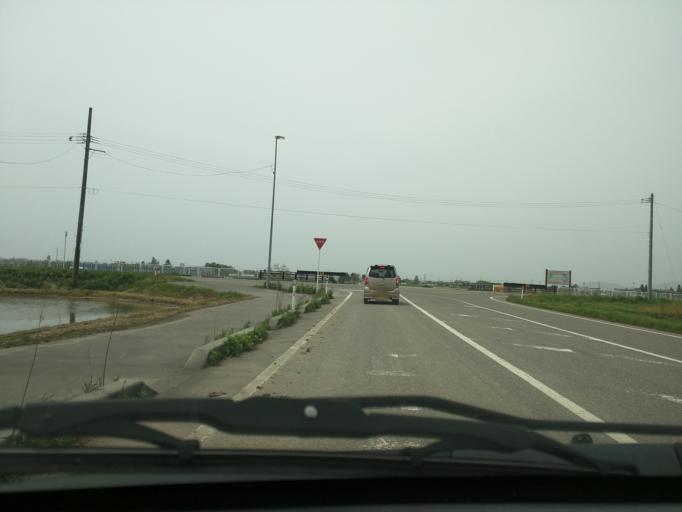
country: JP
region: Niigata
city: Sanjo
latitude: 37.5754
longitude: 138.9416
